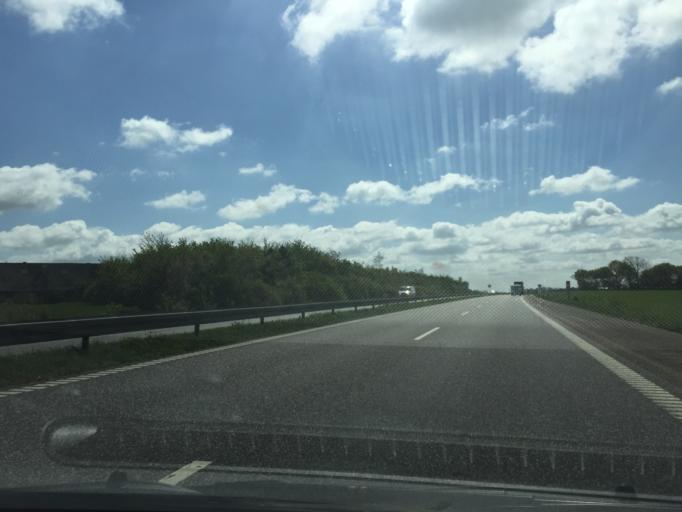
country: DK
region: Zealand
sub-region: Guldborgsund Kommune
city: Norre Alslev
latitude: 54.8802
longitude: 11.9054
